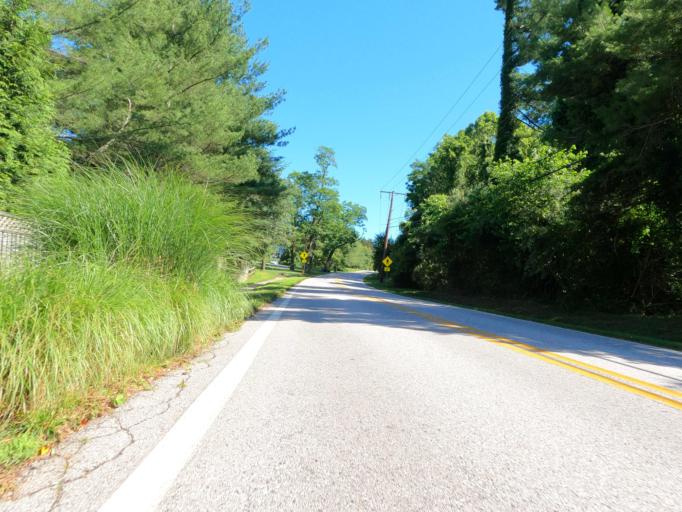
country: US
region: Maryland
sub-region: Howard County
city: Riverside
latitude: 39.2052
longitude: -76.9190
